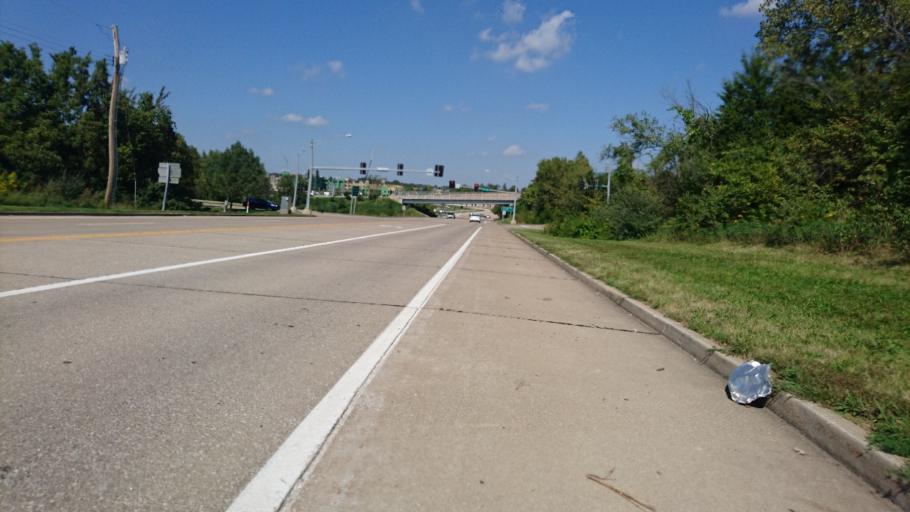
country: US
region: Missouri
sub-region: Saint Louis County
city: Town and Country
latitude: 38.6024
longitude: -90.4551
